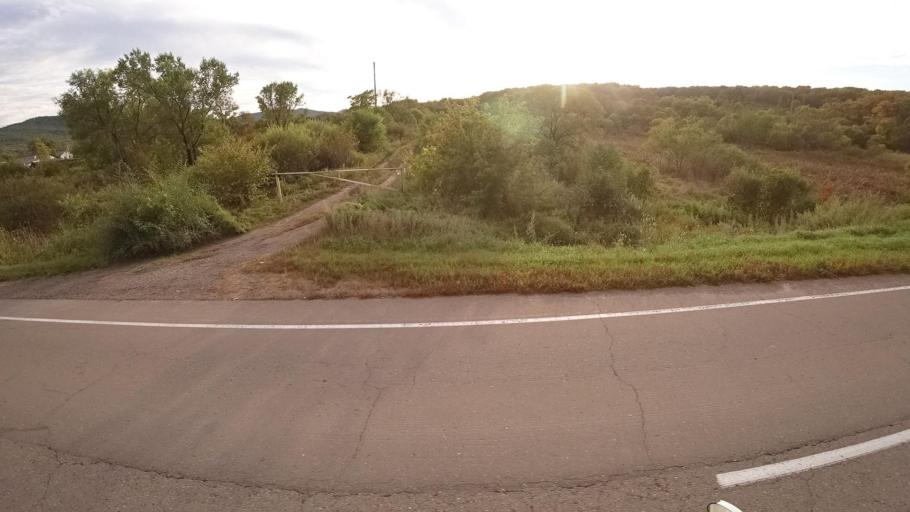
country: RU
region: Primorskiy
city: Yakovlevka
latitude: 44.4216
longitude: 133.4503
